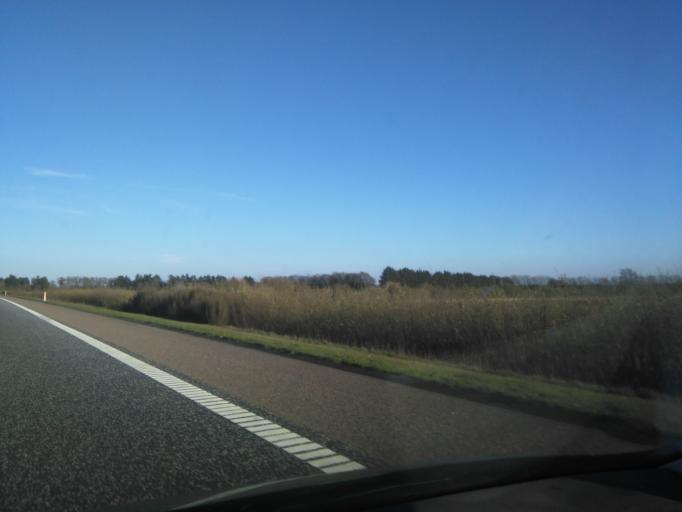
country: DK
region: Central Jutland
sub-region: Herning Kommune
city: Gjellerup Kirkeby
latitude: 56.1224
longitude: 9.0276
